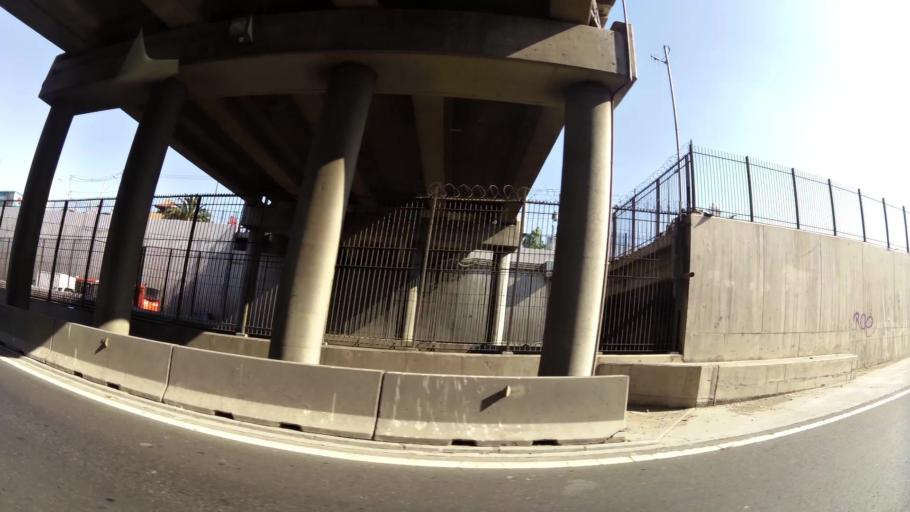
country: CL
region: Santiago Metropolitan
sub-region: Provincia de Santiago
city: La Pintana
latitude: -33.5368
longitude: -70.6658
